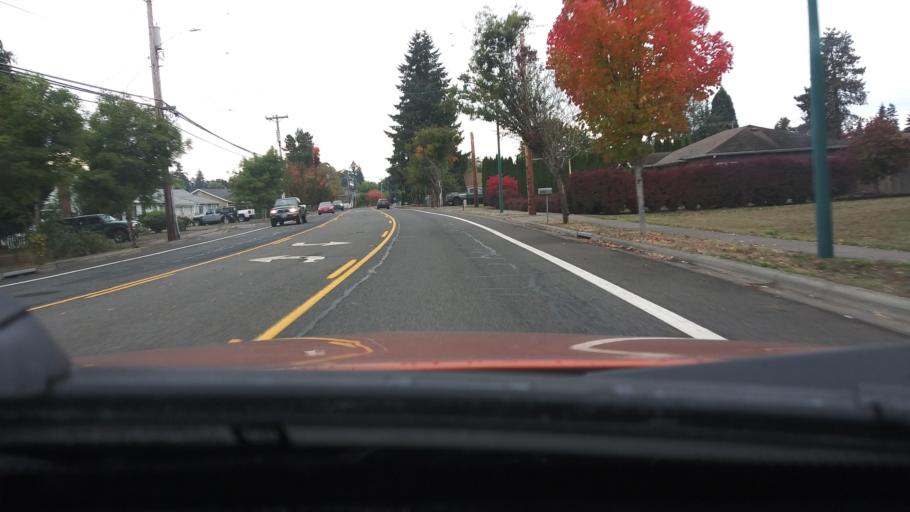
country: US
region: Oregon
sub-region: Washington County
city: Forest Grove
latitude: 45.5320
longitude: -123.1078
